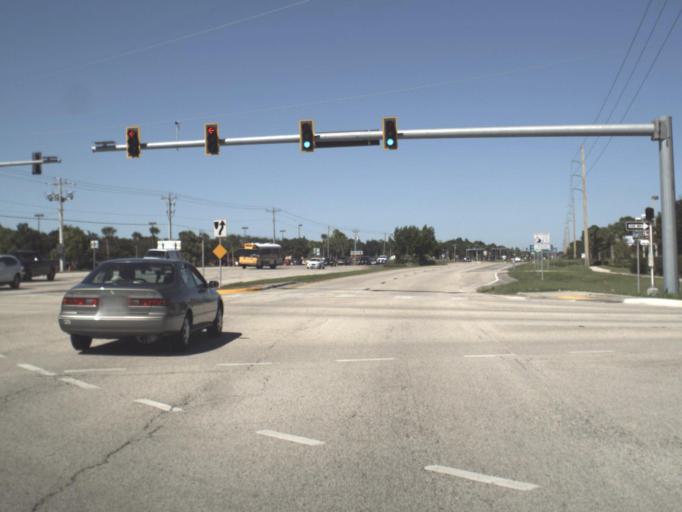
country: US
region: Florida
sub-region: Lee County
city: Palmona Park
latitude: 26.6820
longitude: -81.9015
